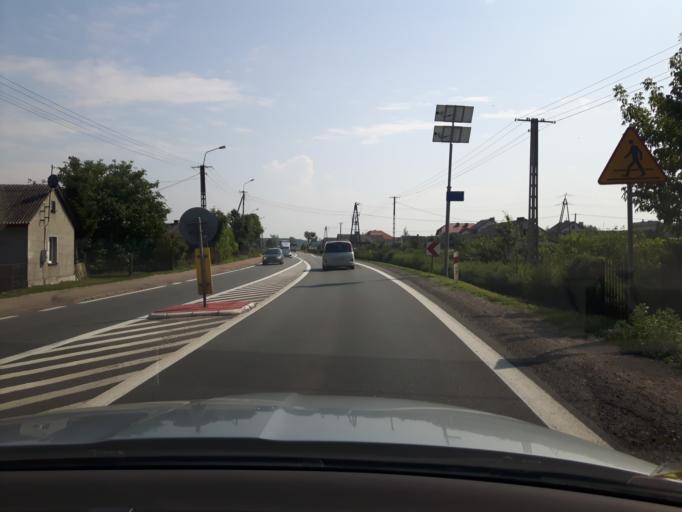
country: PL
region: Masovian Voivodeship
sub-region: Powiat mlawski
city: Strzegowo
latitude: 52.9425
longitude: 20.2818
